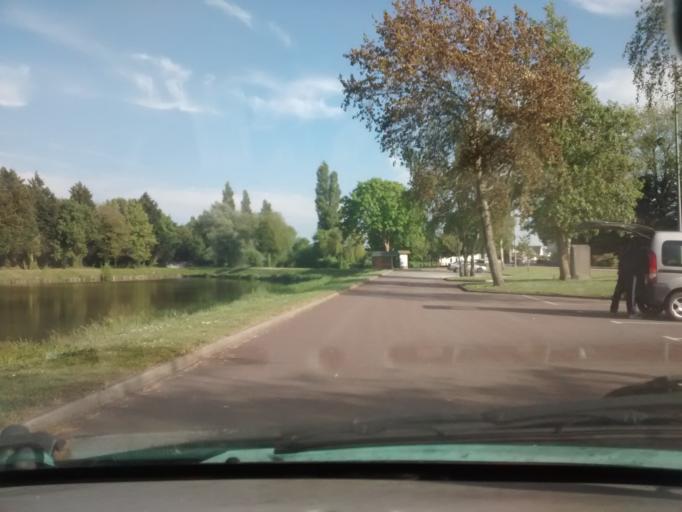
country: FR
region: Lower Normandy
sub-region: Departement de la Manche
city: Lessay
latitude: 49.2223
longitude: -1.5322
